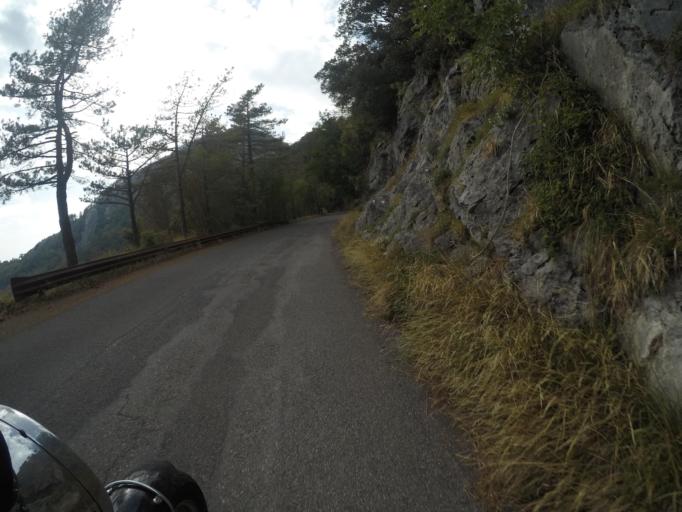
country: IT
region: Tuscany
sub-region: Provincia di Massa-Carrara
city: Fosdinovo
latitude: 44.1236
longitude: 10.0889
